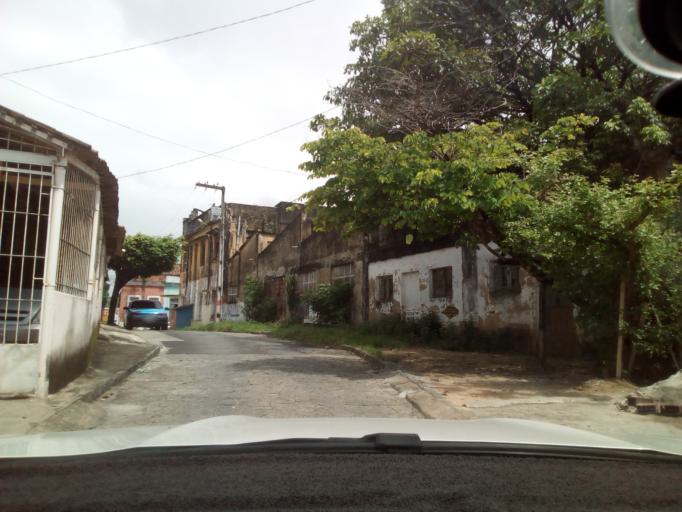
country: BR
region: Paraiba
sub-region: Joao Pessoa
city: Joao Pessoa
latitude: -7.1205
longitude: -34.8918
